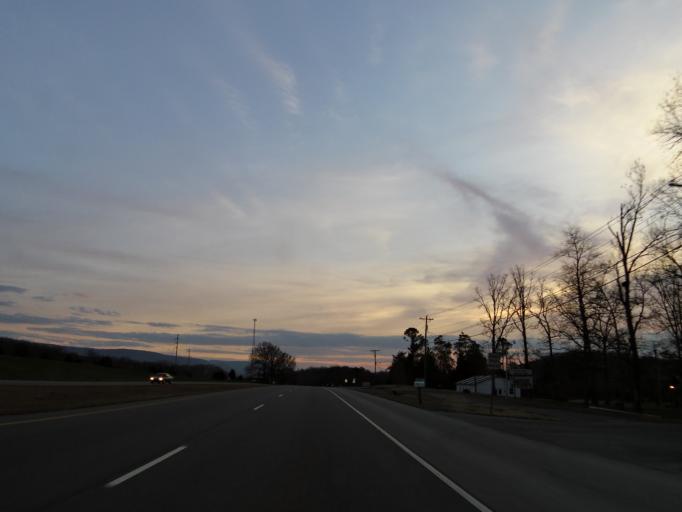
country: US
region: Tennessee
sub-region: McMinn County
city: Etowah
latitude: 35.3629
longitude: -84.5145
